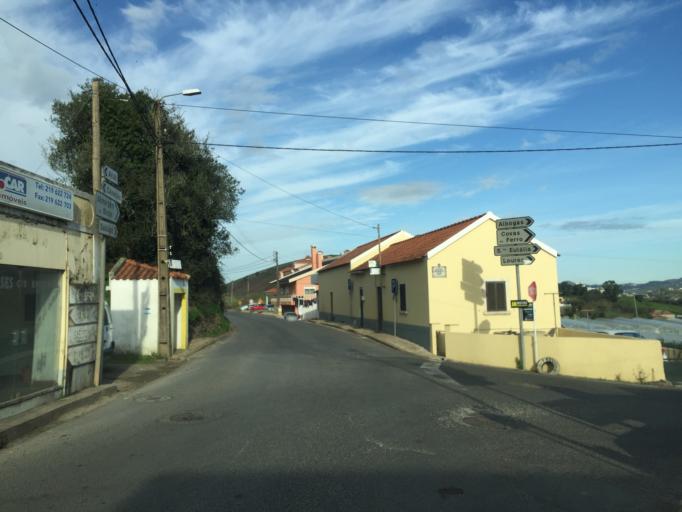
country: PT
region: Lisbon
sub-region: Sintra
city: Almargem
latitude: 38.8484
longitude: -9.2622
